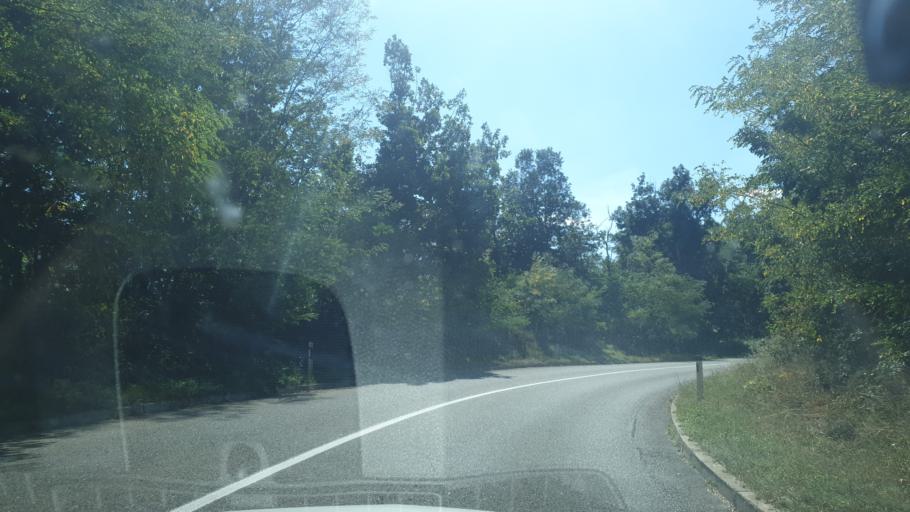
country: RS
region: Central Serbia
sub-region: Kolubarski Okrug
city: Mionica
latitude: 44.1707
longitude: 19.9993
